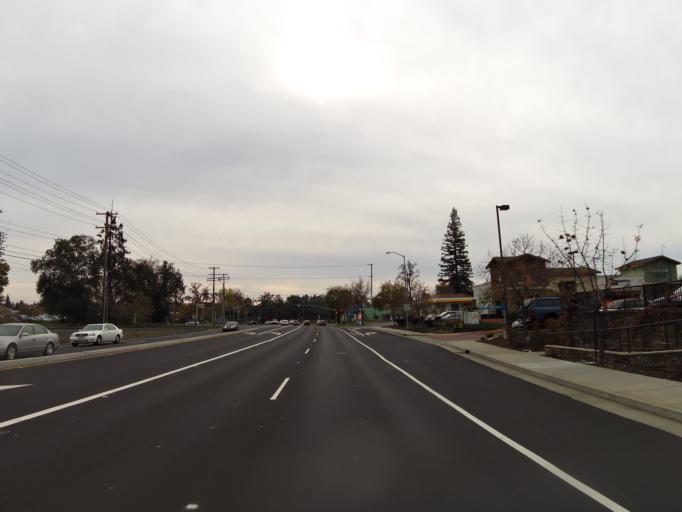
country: US
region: California
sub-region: Sacramento County
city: Folsom
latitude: 38.6560
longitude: -121.1823
